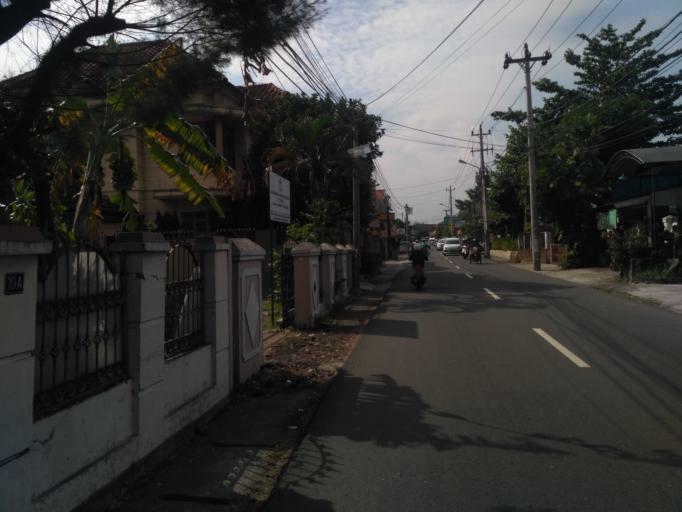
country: ID
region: Daerah Istimewa Yogyakarta
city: Depok
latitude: -7.7807
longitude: 110.4085
